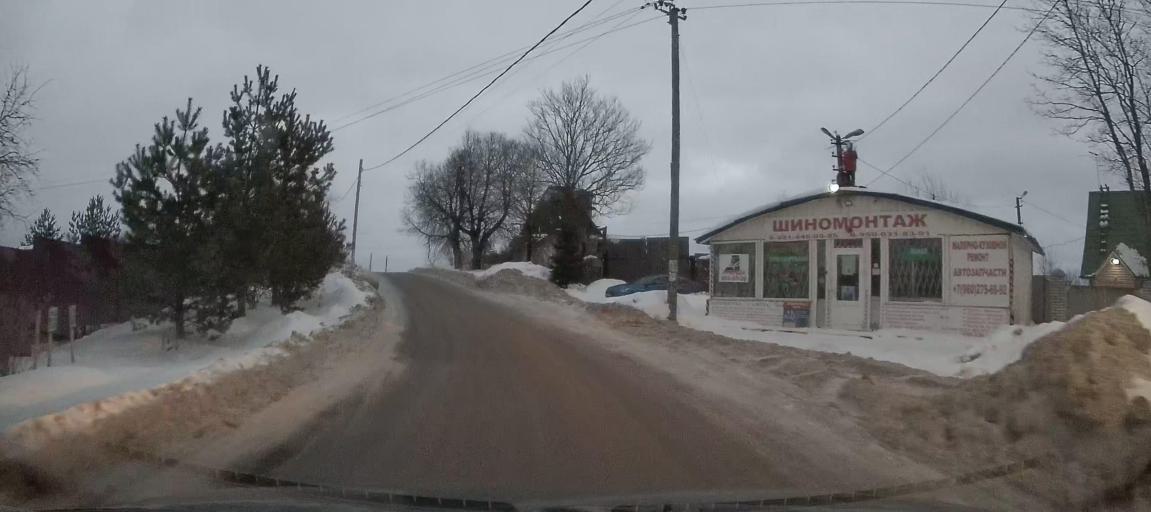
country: RU
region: Leningrad
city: Taytsy
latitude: 59.6970
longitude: 30.1401
